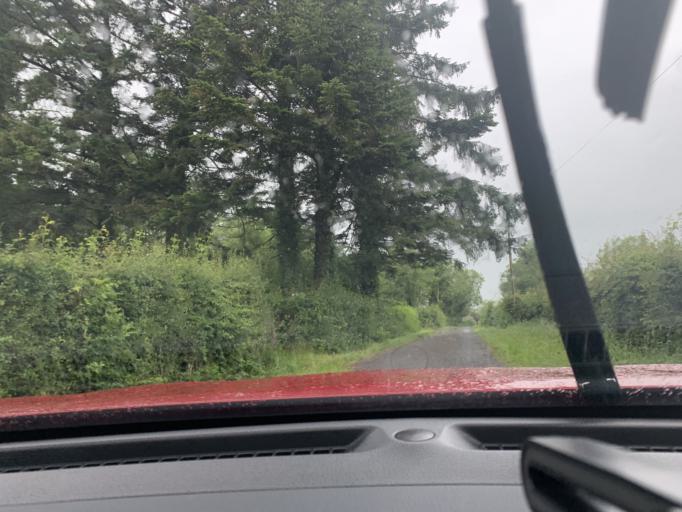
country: GB
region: Northern Ireland
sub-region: Fermanagh District
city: Enniskillen
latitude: 54.2679
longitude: -7.7435
